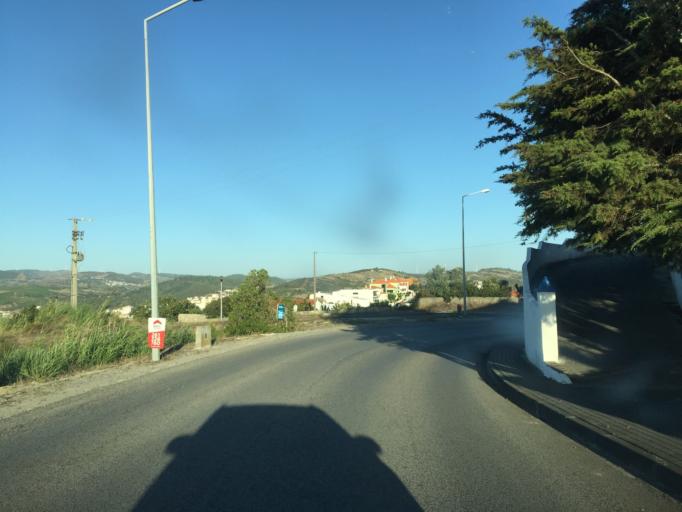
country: PT
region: Lisbon
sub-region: Torres Vedras
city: Torres Vedras
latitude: 39.0904
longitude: -9.2735
